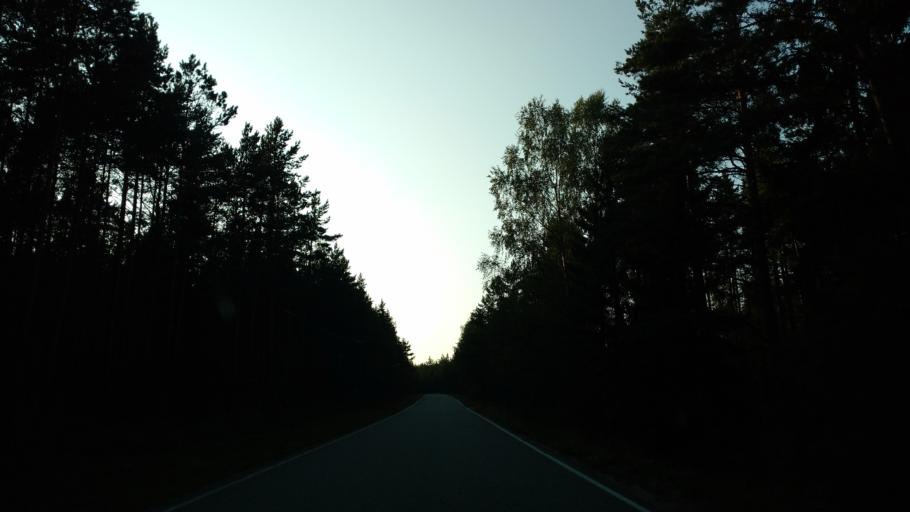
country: FI
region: Varsinais-Suomi
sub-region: Salo
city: Saerkisalo
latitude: 60.2036
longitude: 22.9311
